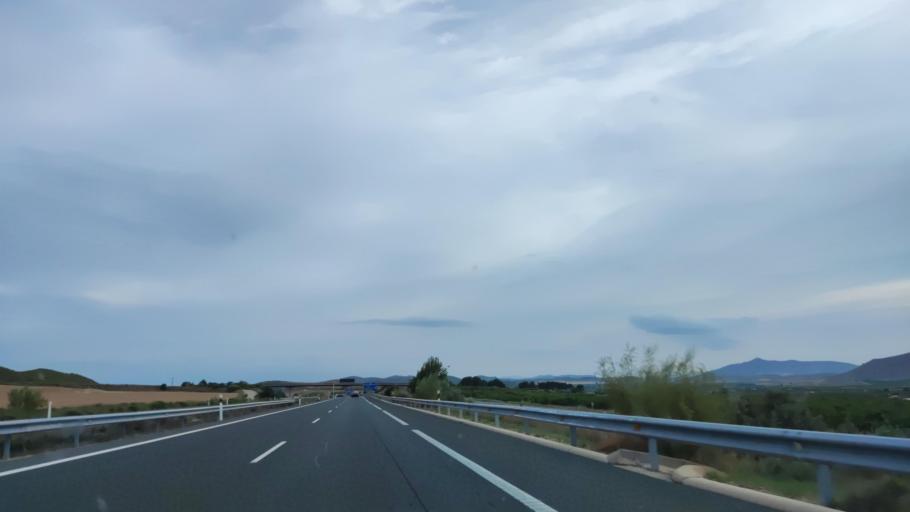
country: ES
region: Castille-La Mancha
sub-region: Provincia de Albacete
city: Tobarra
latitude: 38.6189
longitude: -1.6773
